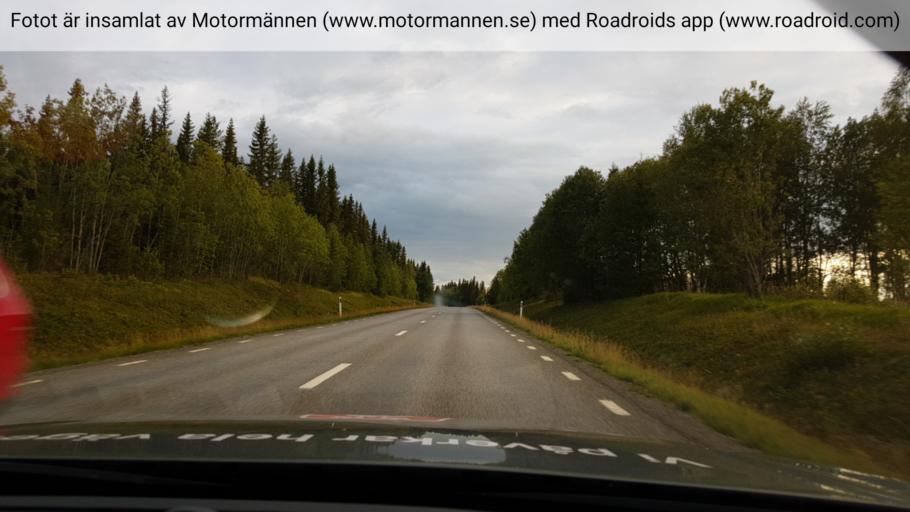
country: SE
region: Jaemtland
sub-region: OEstersunds Kommun
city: Lit
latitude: 63.4419
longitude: 15.1357
